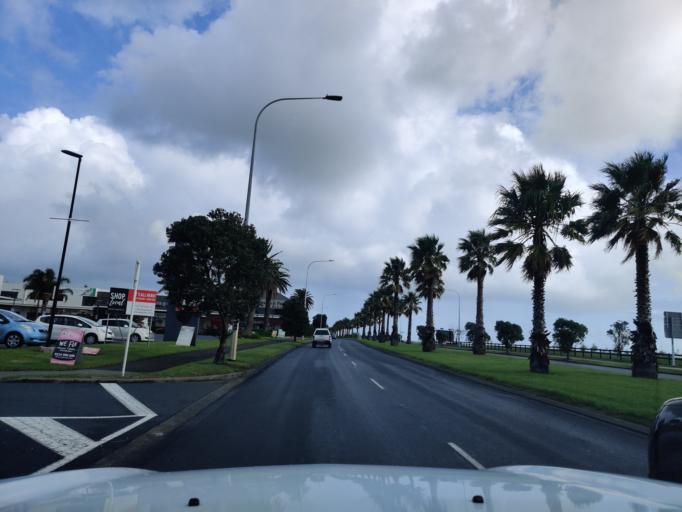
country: NZ
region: Auckland
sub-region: Auckland
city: Manukau City
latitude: -36.9644
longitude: 174.9019
